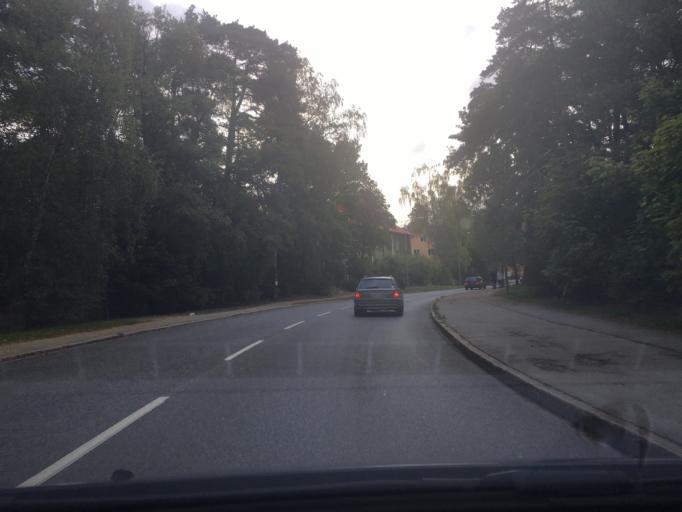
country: SE
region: Stockholm
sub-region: Stockholms Kommun
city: Bromma
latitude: 59.3286
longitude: 17.9642
